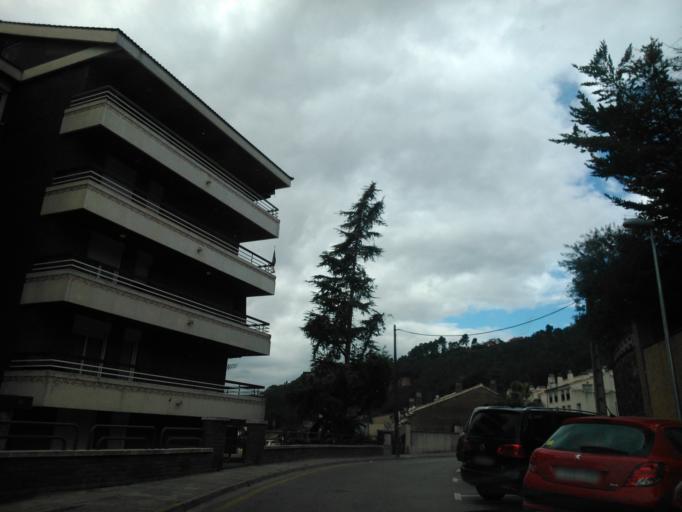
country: ES
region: Catalonia
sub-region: Provincia de Barcelona
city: Cervello
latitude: 41.4143
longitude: 1.9688
